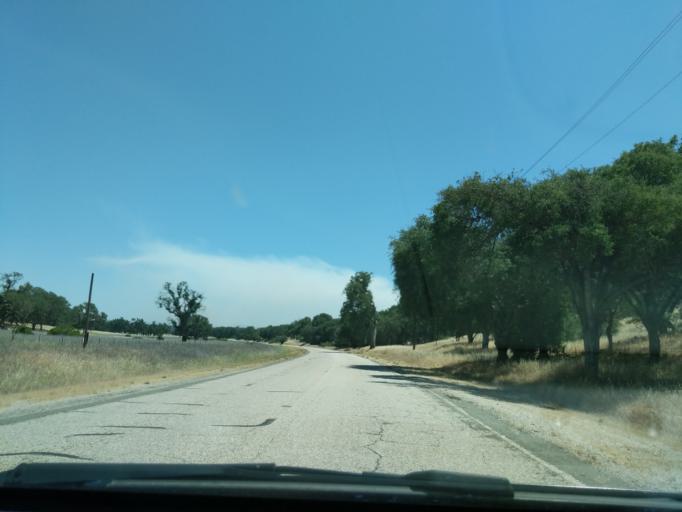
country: US
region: California
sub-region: Monterey County
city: King City
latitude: 36.0461
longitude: -121.1830
